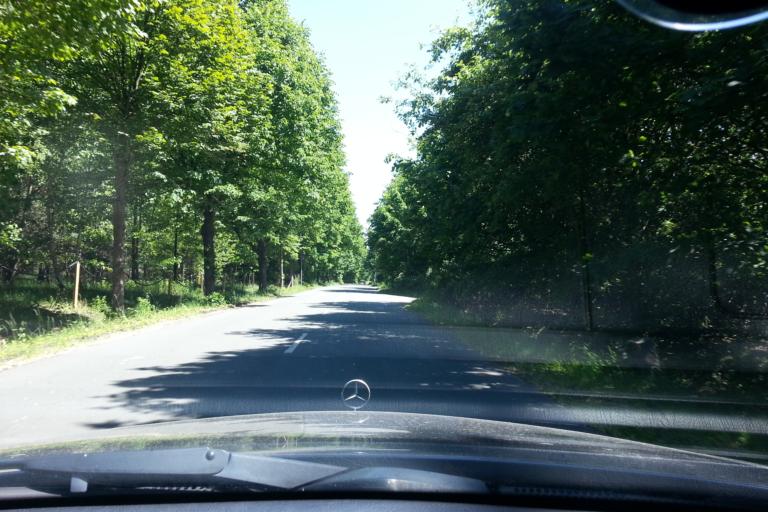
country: DE
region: North Rhine-Westphalia
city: Marl
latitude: 51.6917
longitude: 7.1108
